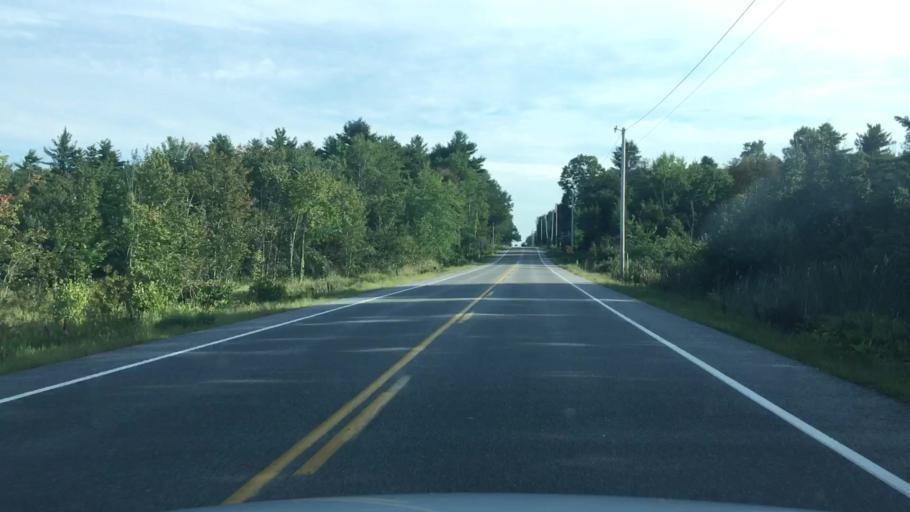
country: US
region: Maine
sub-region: Cumberland County
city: North Windham
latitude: 43.8164
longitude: -70.4413
